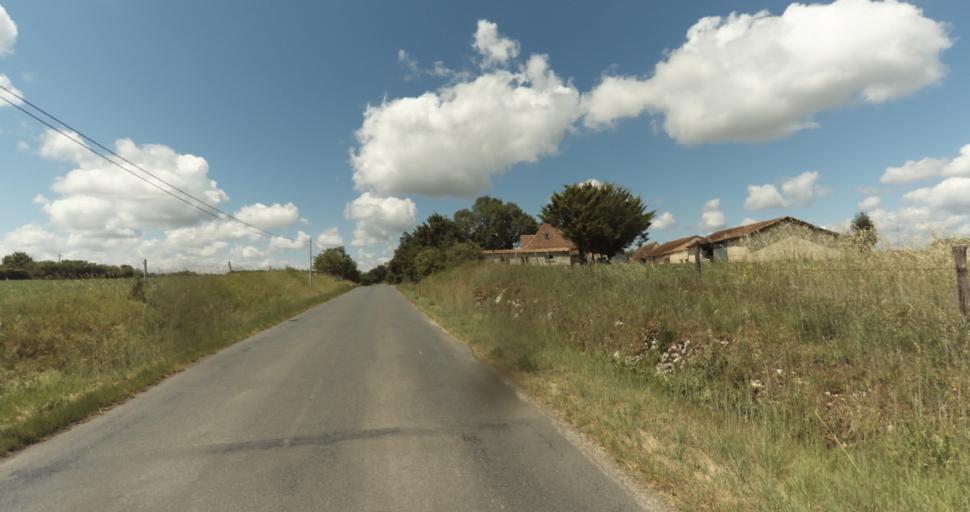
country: FR
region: Aquitaine
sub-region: Departement de la Dordogne
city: Beaumont-du-Perigord
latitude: 44.7538
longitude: 0.7038
